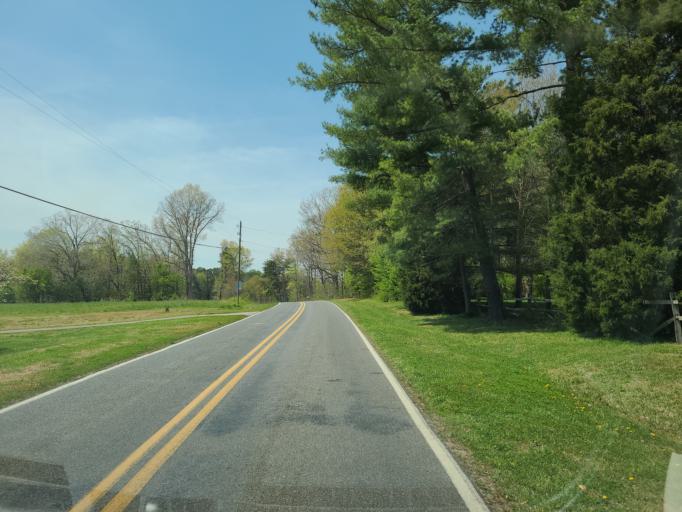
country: US
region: North Carolina
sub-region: Cleveland County
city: Shelby
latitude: 35.2582
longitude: -81.4897
